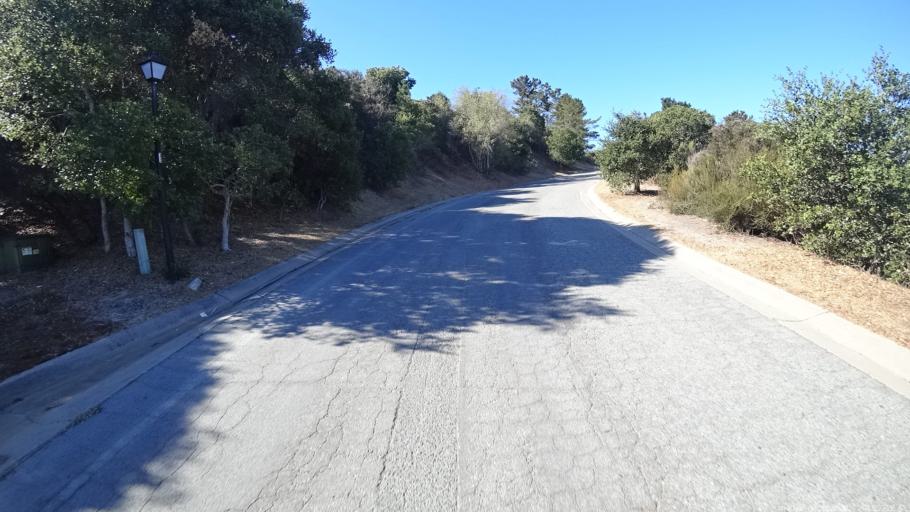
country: US
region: California
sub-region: Monterey County
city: Carmel Valley Village
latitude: 36.5649
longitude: -121.7369
